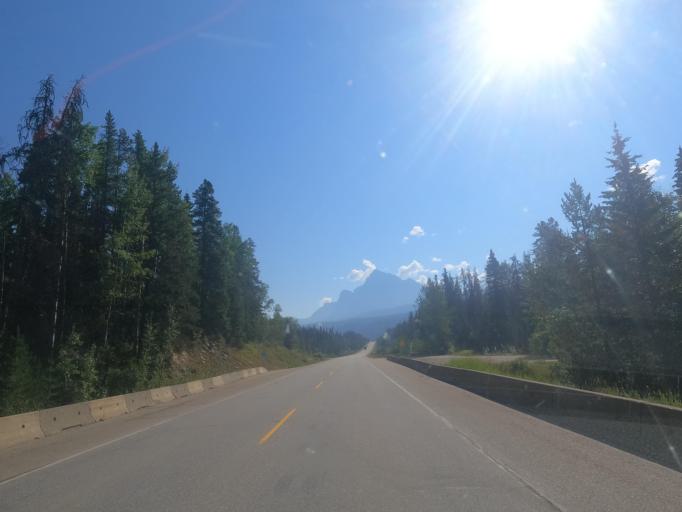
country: CA
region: Alberta
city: Jasper Park Lodge
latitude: 52.8525
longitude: -118.6054
